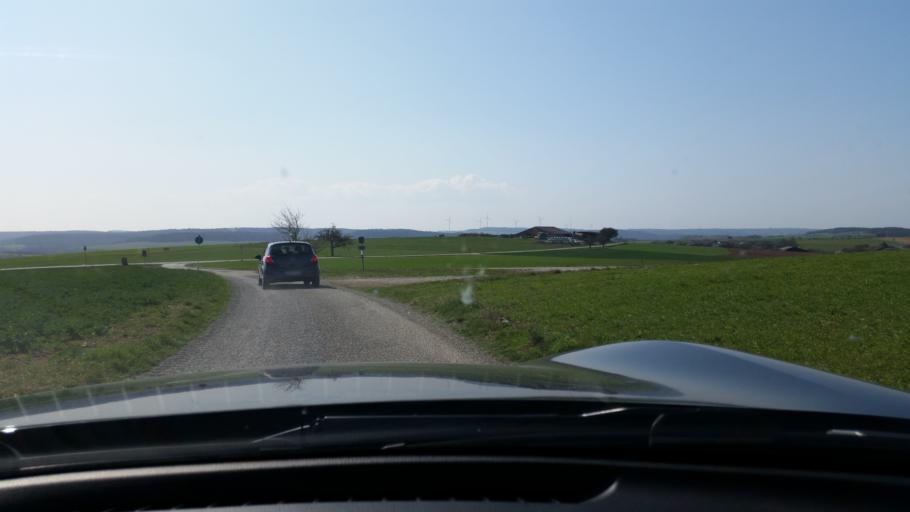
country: DE
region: Baden-Wuerttemberg
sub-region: Regierungsbezirk Stuttgart
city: Krautheim
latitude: 49.4020
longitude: 9.6425
